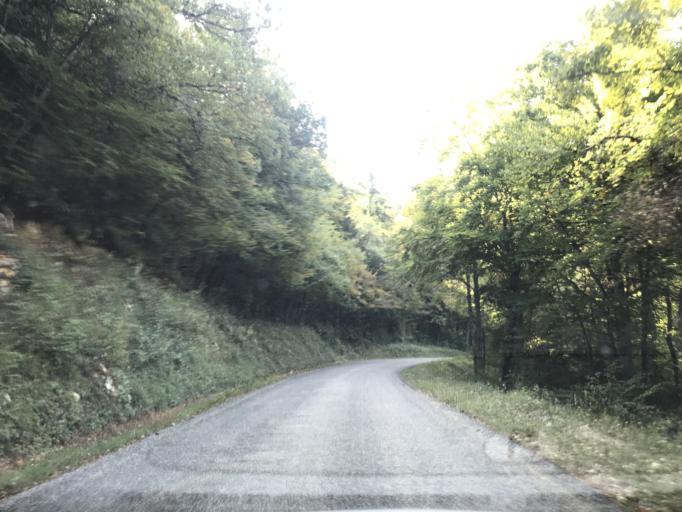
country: FR
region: Rhone-Alpes
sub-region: Departement de la Savoie
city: Novalaise
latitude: 45.6430
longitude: 5.7989
